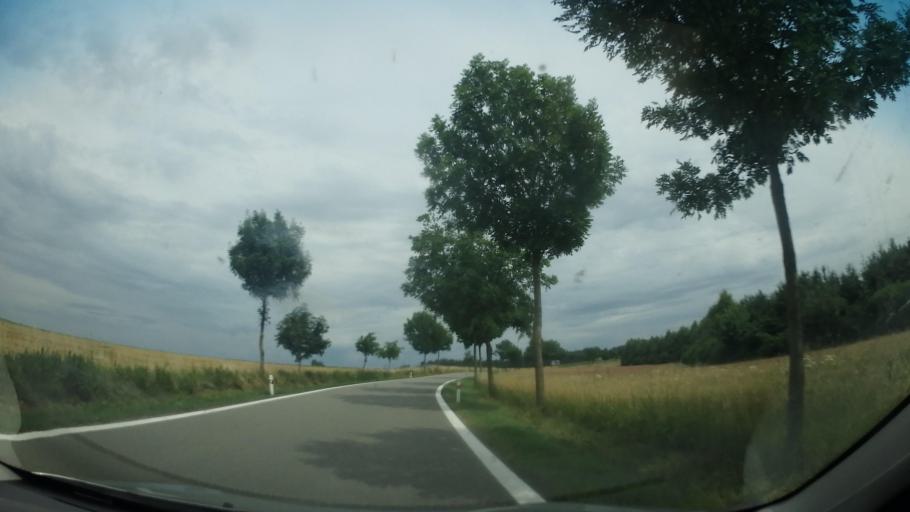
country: CZ
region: Vysocina
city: Bystrice nad Pernstejnem
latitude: 49.4613
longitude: 16.2306
